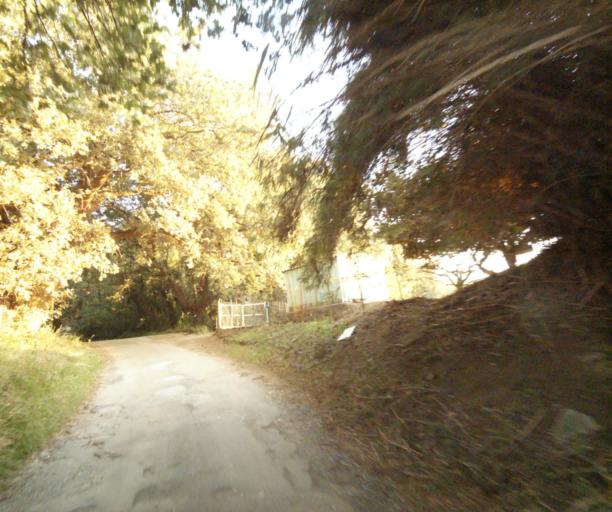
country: FR
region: Languedoc-Roussillon
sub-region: Departement des Pyrenees-Orientales
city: Argelers
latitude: 42.5745
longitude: 3.0117
